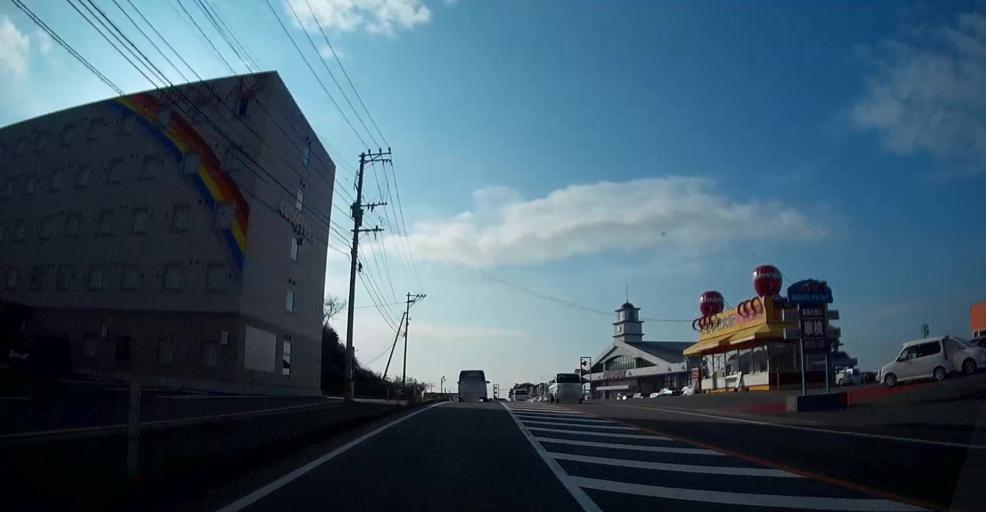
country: JP
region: Kumamoto
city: Yatsushiro
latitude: 32.5718
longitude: 130.4182
